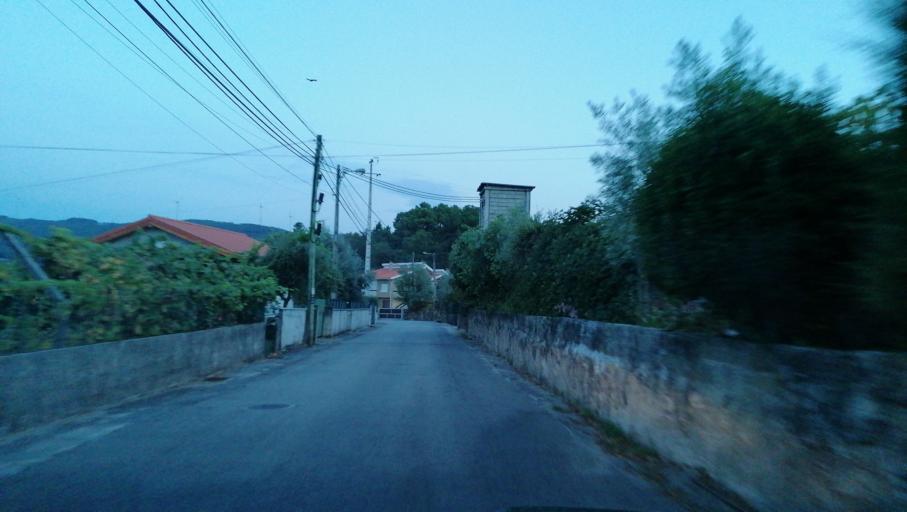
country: PT
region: Vila Real
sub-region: Vila Pouca de Aguiar
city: Vila Pouca de Aguiar
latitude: 41.5492
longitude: -7.6203
